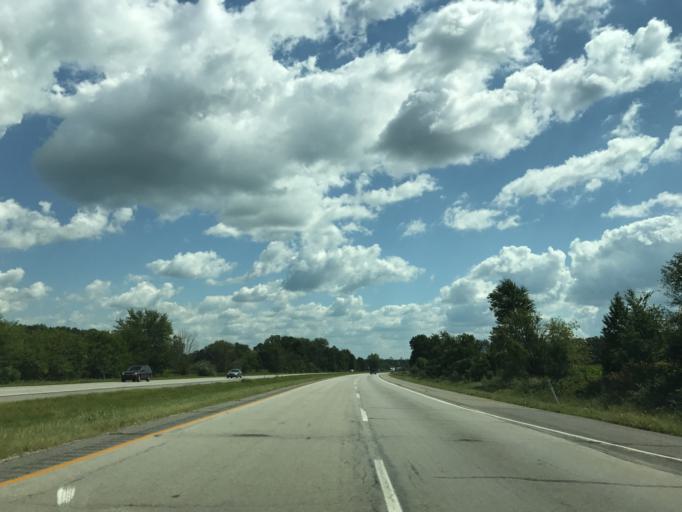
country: US
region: Indiana
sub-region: Marshall County
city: Plymouth
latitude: 41.3645
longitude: -86.3867
